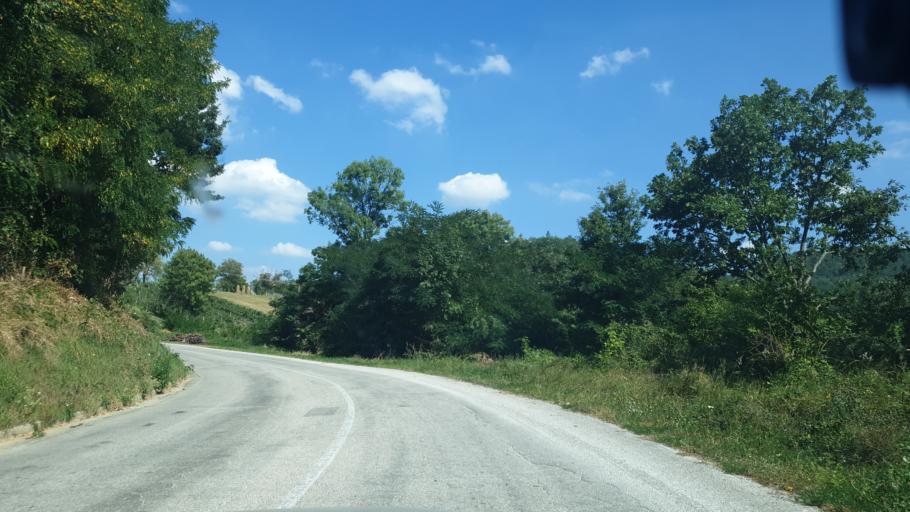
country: RS
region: Central Serbia
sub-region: Zlatiborski Okrug
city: Kosjeric
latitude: 44.0147
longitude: 20.0331
